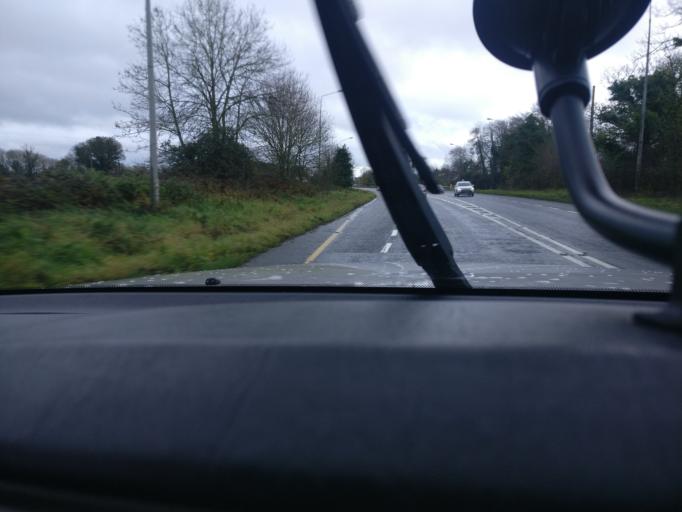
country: IE
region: Leinster
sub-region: Kildare
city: Kilcock
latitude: 53.4126
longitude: -6.7141
